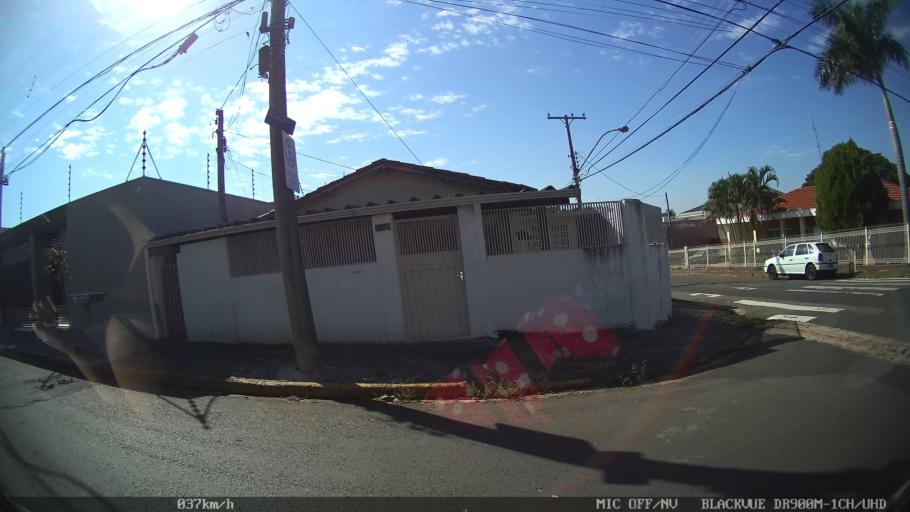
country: BR
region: Sao Paulo
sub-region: Americana
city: Americana
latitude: -22.7520
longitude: -47.3266
